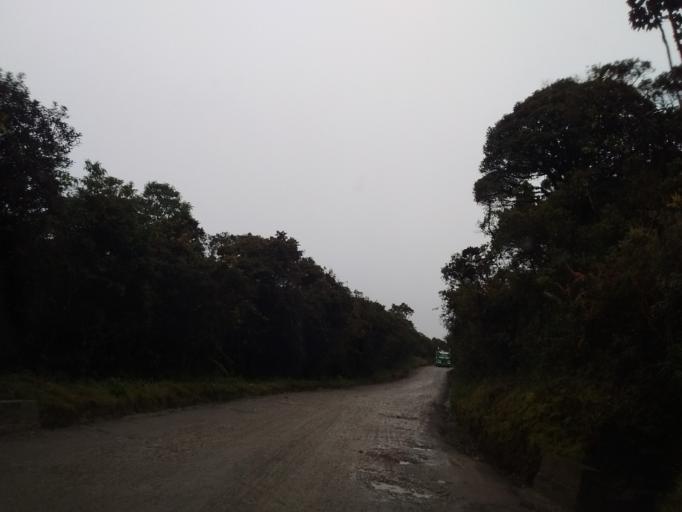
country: CO
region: Cauca
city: Paispamba
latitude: 2.1458
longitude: -76.4312
